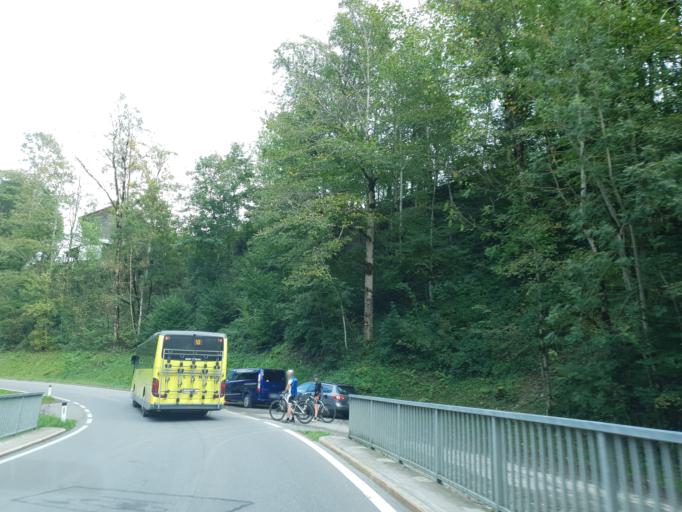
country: AT
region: Vorarlberg
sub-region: Politischer Bezirk Bregenz
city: Au
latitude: 47.3180
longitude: 9.9624
